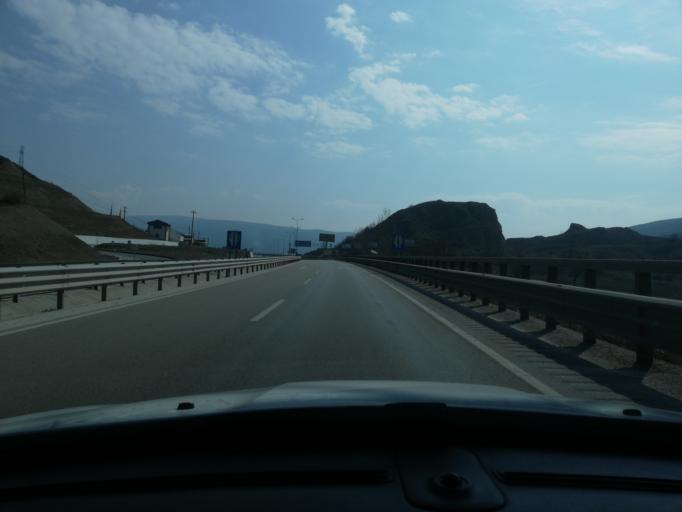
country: TR
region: Cankiri
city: Ilgaz
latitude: 40.9069
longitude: 33.6165
